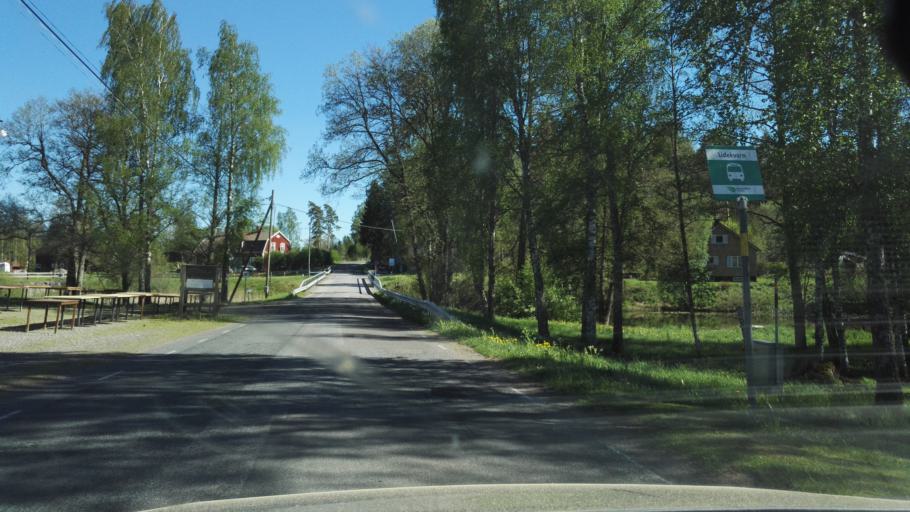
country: SE
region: Kronoberg
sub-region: Vaxjo Kommun
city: Rottne
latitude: 57.0828
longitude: 14.8200
